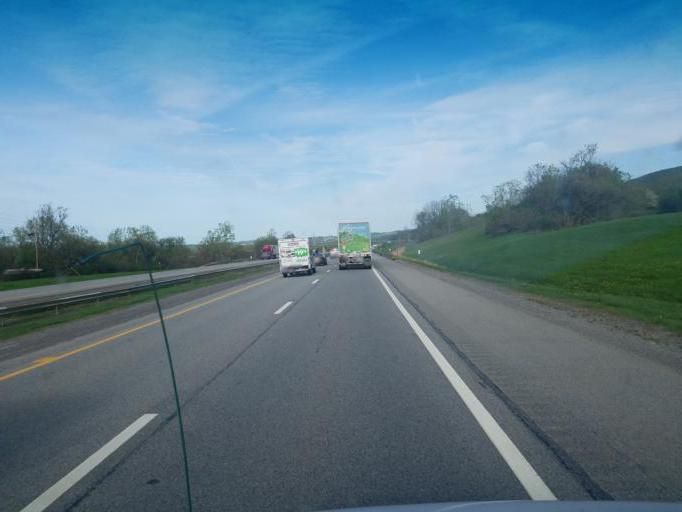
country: US
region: New York
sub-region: Herkimer County
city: Herkimer
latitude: 43.0145
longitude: -74.9543
